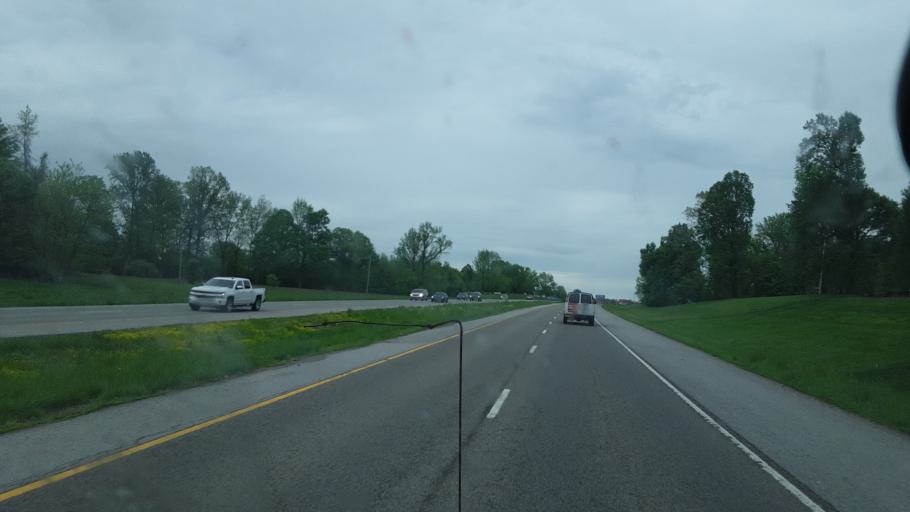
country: US
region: Illinois
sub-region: Jackson County
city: Murphysboro
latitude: 37.7638
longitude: -89.2881
